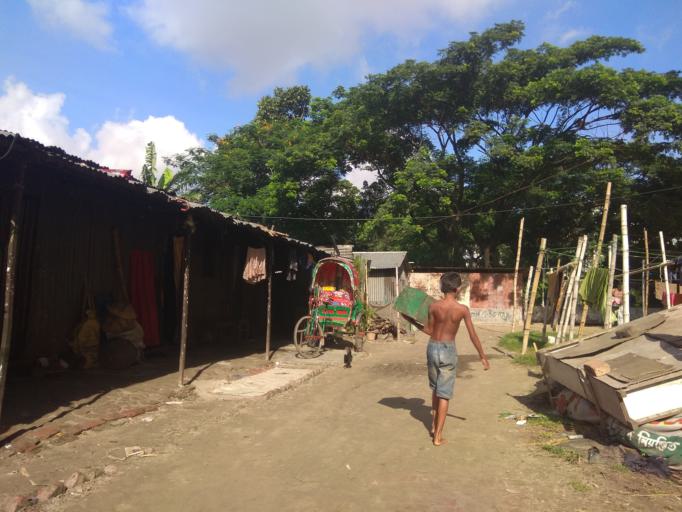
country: BD
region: Dhaka
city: Paltan
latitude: 23.8053
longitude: 90.3870
